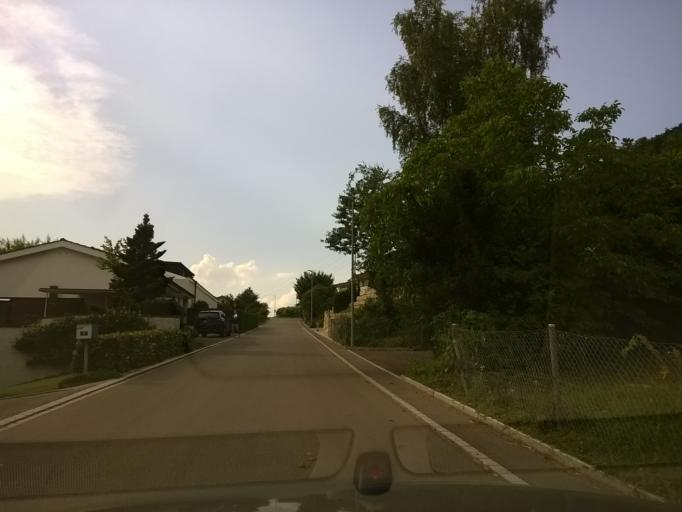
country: CH
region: Zurich
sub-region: Bezirk Buelach
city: Embrach / Embrach (Dorfkern)
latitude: 47.4900
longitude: 8.6146
